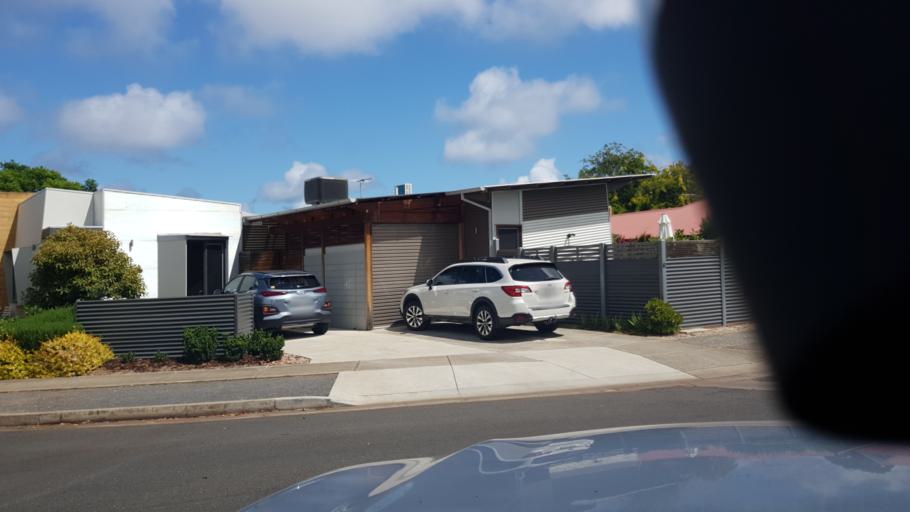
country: AU
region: South Australia
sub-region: Adelaide
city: Brighton
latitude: -35.0197
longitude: 138.5317
